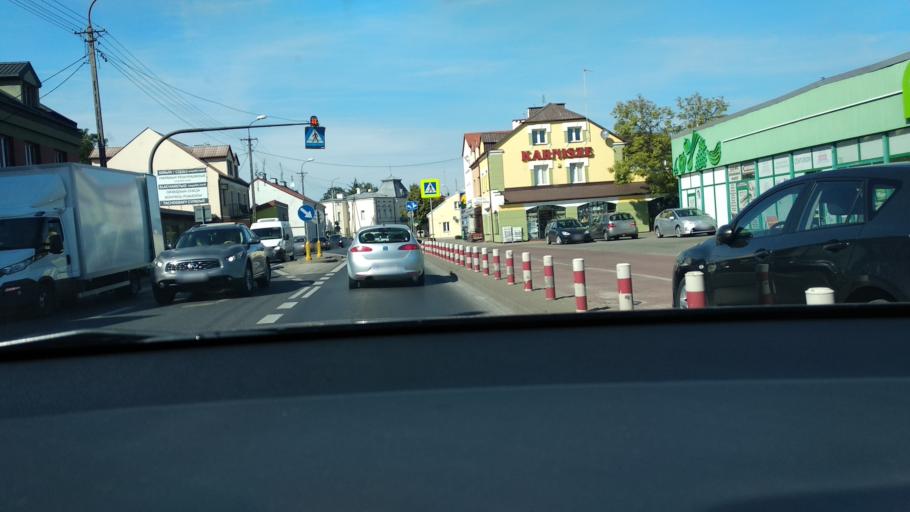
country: PL
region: Masovian Voivodeship
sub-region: Powiat pultuski
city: Pultusk
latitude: 52.7014
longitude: 21.0855
